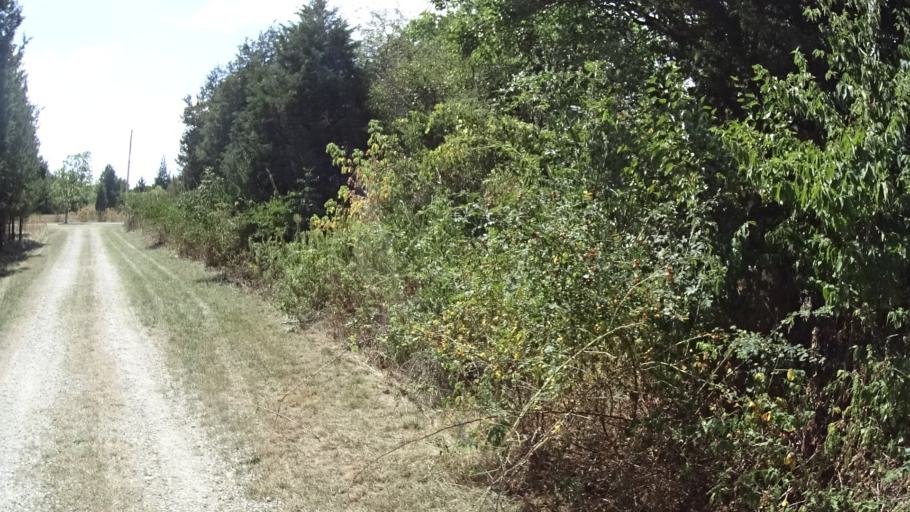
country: US
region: Ohio
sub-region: Erie County
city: Sandusky
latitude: 41.6086
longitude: -82.6936
